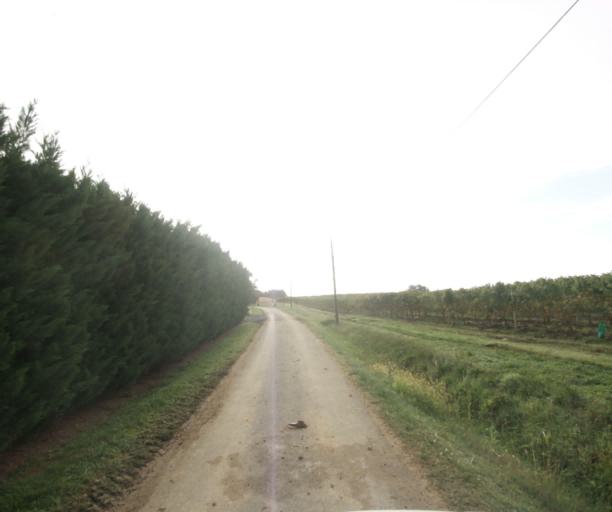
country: FR
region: Midi-Pyrenees
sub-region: Departement du Gers
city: Nogaro
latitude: 43.8246
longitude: -0.0543
